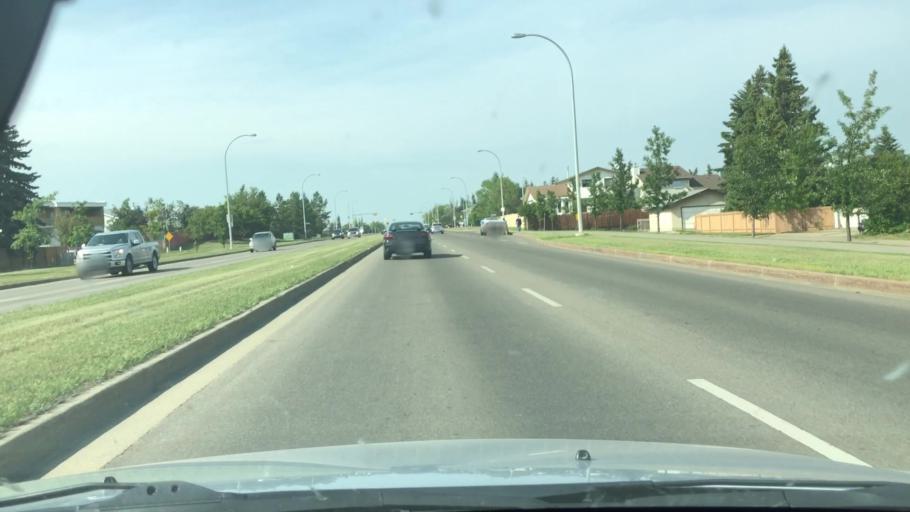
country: CA
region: Alberta
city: Edmonton
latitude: 53.6132
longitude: -113.4428
